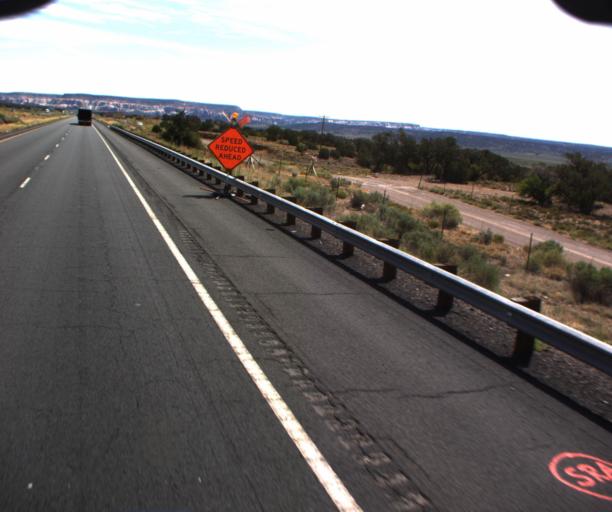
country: US
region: Arizona
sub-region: Apache County
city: Houck
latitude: 35.2988
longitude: -109.1333
